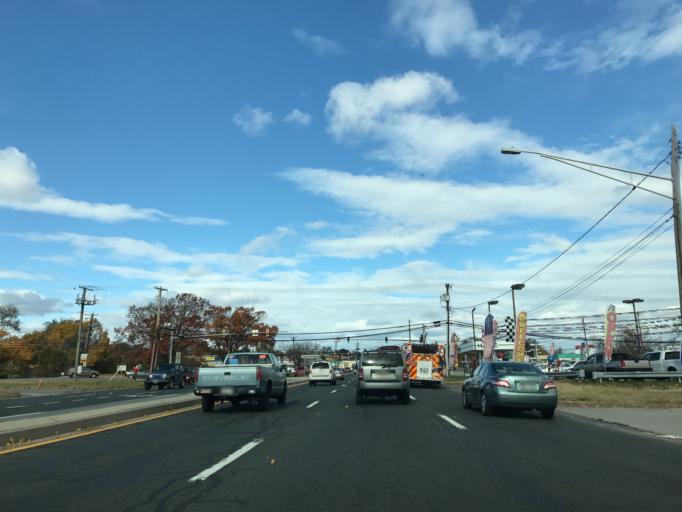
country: US
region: Maryland
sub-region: Anne Arundel County
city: Glen Burnie
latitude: 39.1872
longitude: -76.6130
